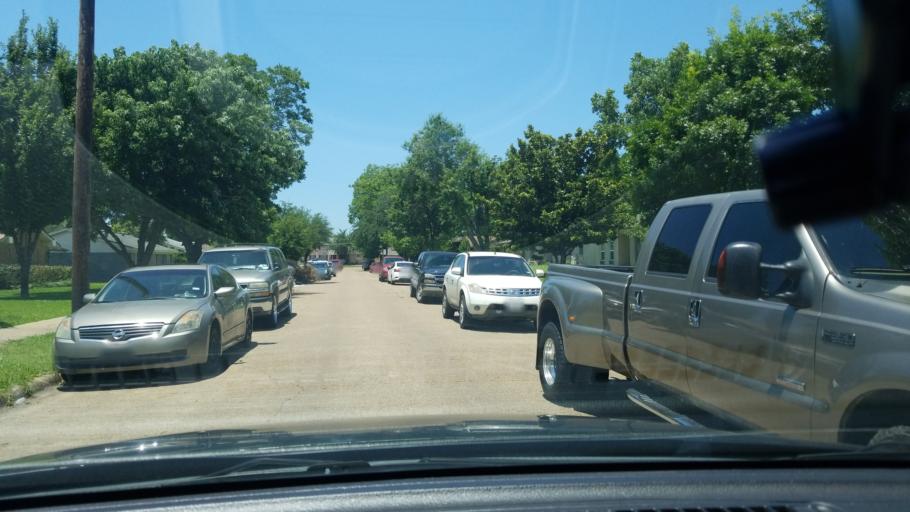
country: US
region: Texas
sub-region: Dallas County
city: Mesquite
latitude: 32.7949
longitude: -96.6496
